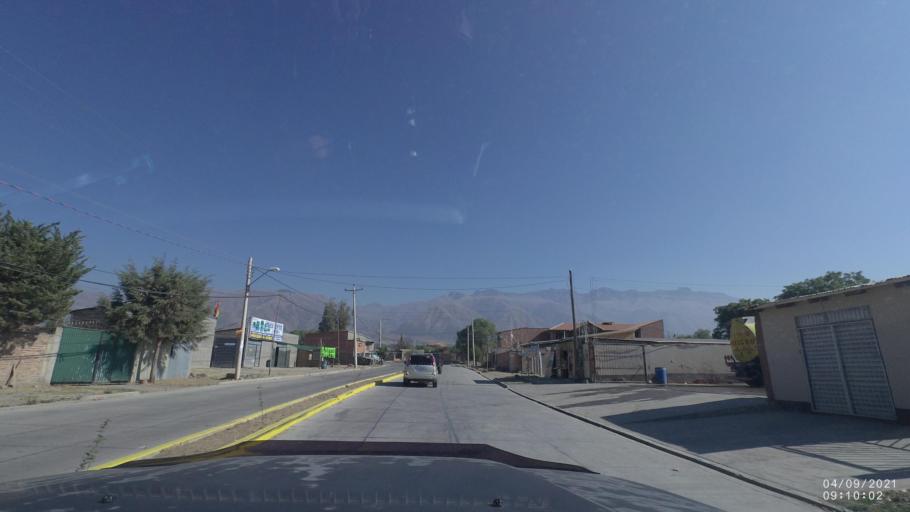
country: BO
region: Cochabamba
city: Sipe Sipe
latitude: -17.3939
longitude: -66.3296
